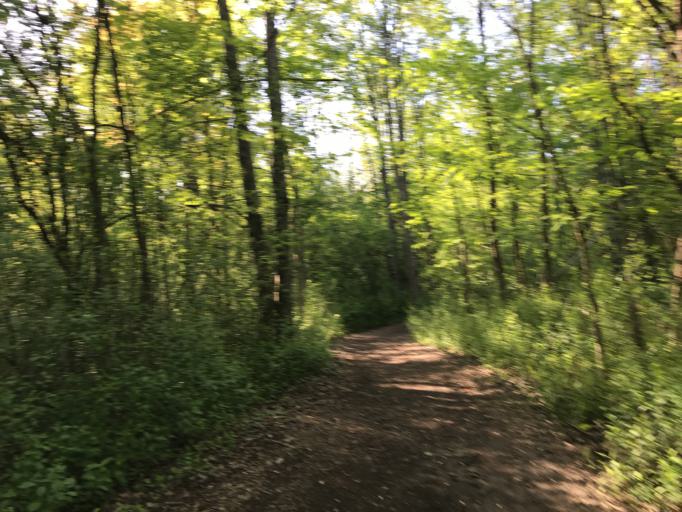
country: US
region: Michigan
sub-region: Oakland County
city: Farmington Hills
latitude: 42.4926
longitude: -83.3810
